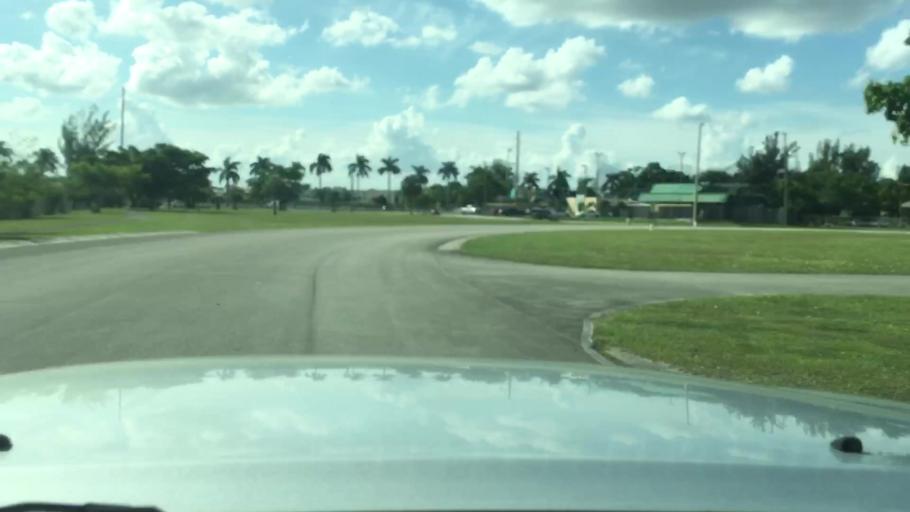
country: US
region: Florida
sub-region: Miami-Dade County
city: University Park
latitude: 25.7472
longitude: -80.3815
